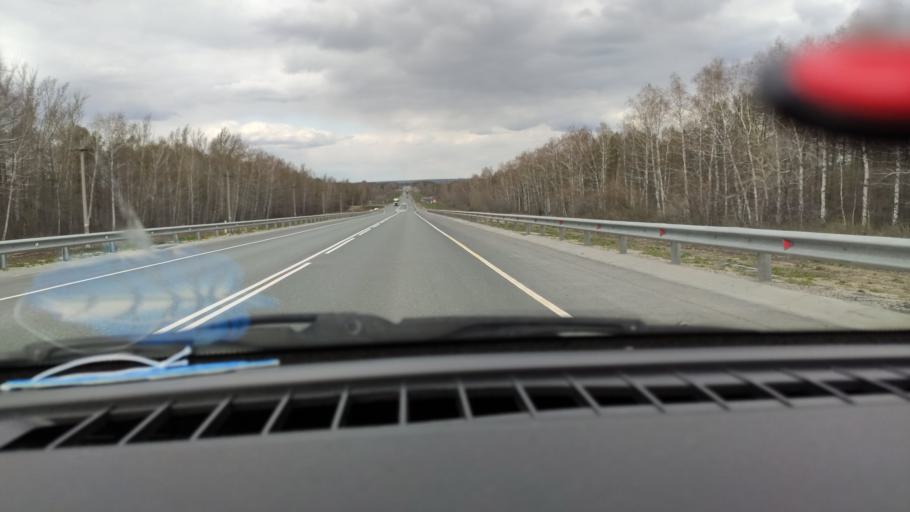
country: RU
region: Saratov
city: Shikhany
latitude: 52.1521
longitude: 47.1857
